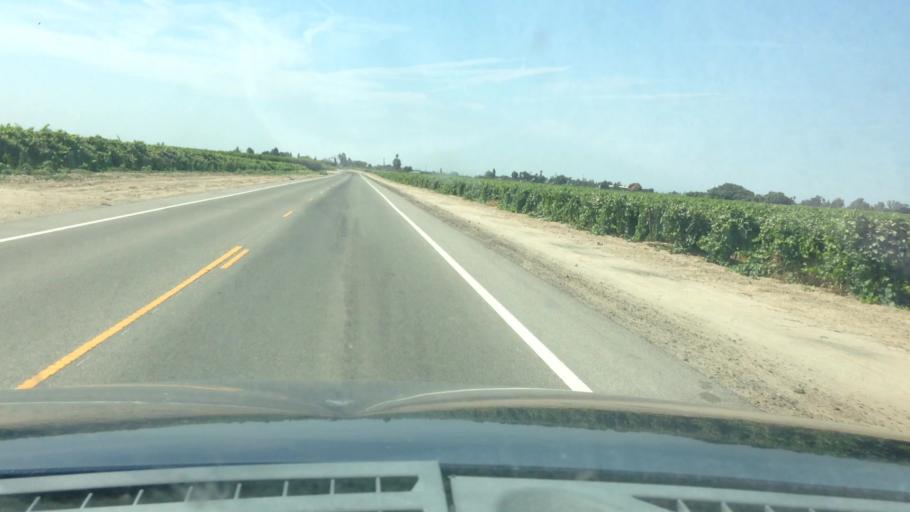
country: US
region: California
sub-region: Fresno County
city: Parlier
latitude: 36.5826
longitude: -119.5571
